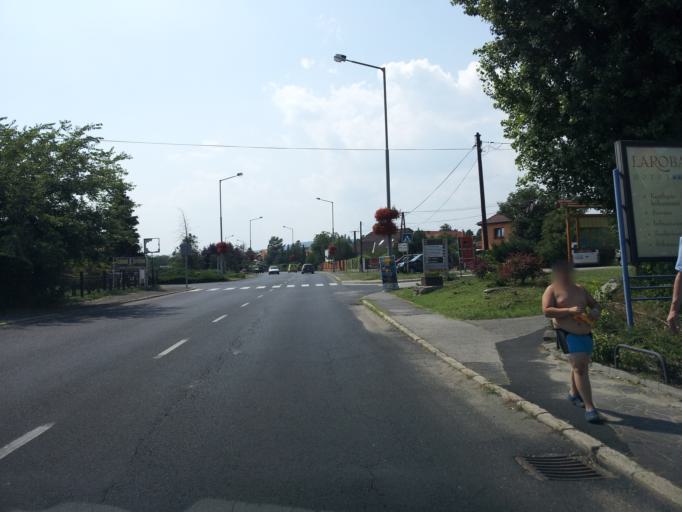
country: HU
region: Veszprem
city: Csopak
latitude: 46.9856
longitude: 17.9764
